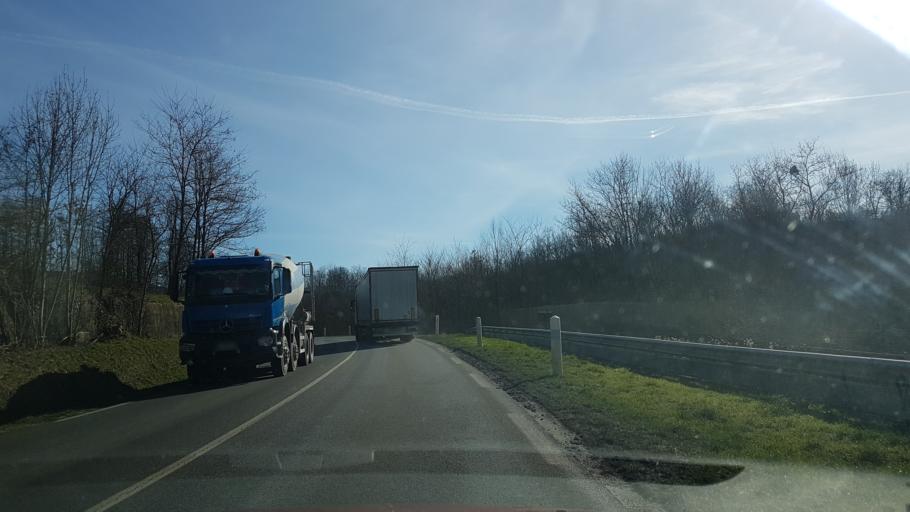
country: FR
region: Rhone-Alpes
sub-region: Departement de la Haute-Savoie
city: Frangy
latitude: 46.0197
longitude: 5.9134
